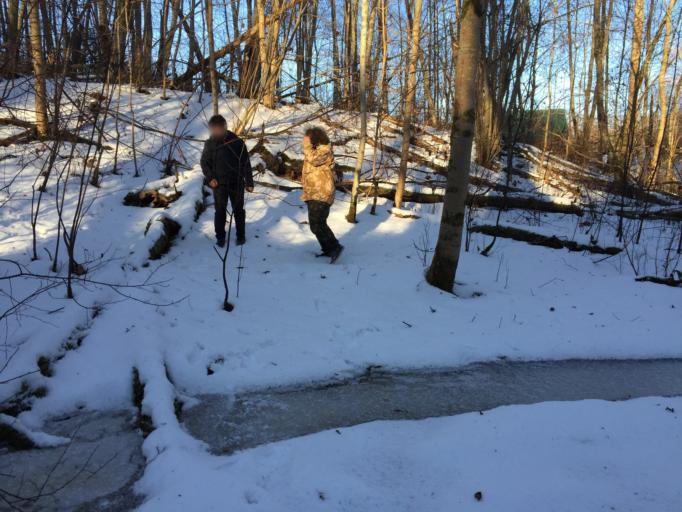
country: LV
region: Lielvarde
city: Lielvarde
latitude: 56.6760
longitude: 24.8780
